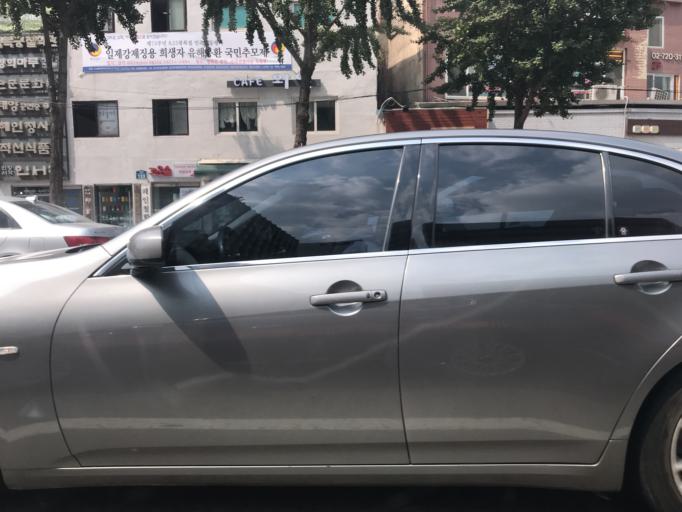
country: KR
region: Seoul
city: Seoul
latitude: 37.5757
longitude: 126.9739
